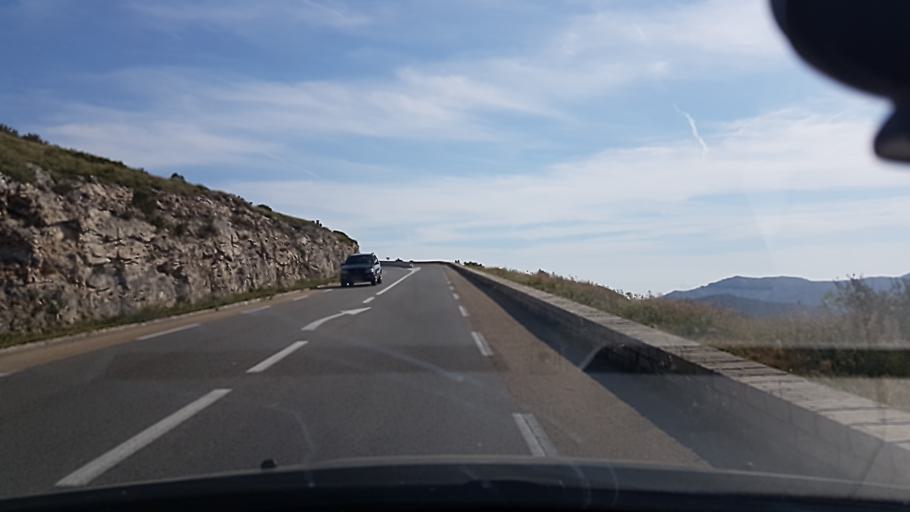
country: FR
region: Provence-Alpes-Cote d'Azur
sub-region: Departement des Bouches-du-Rhone
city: Marseille 09
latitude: 43.2412
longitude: 5.4527
